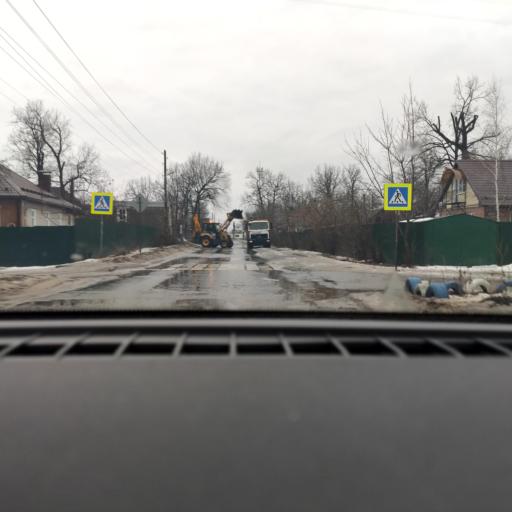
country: RU
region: Voronezj
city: Somovo
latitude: 51.7359
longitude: 39.3570
